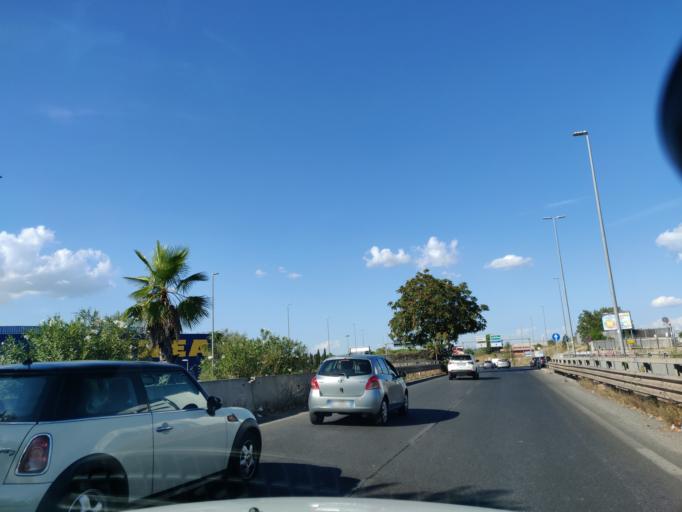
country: IT
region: Latium
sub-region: Citta metropolitana di Roma Capitale
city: Colle Verde
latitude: 41.9711
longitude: 12.5425
